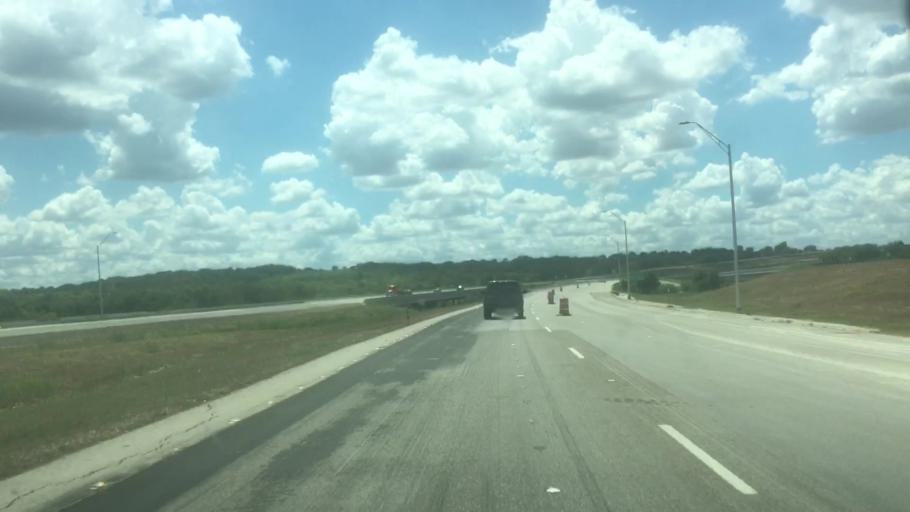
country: US
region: Texas
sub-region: Caldwell County
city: Lockhart
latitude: 29.8621
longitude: -97.7083
